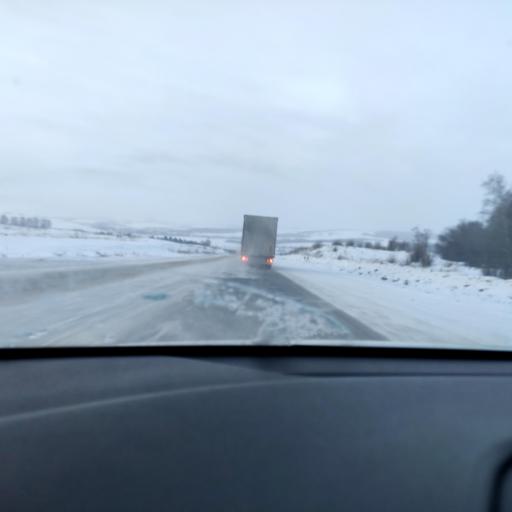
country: RU
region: Tatarstan
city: Sviyazhsk
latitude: 55.6301
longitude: 48.7698
